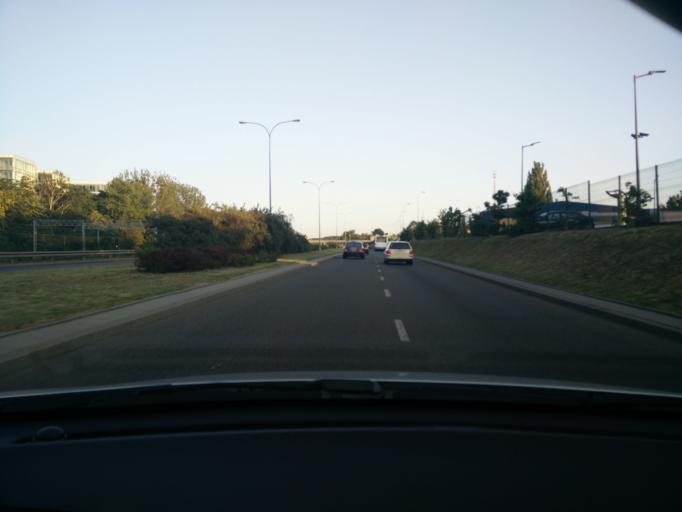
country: PL
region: Pomeranian Voivodeship
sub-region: Gdynia
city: Gdynia
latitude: 54.4947
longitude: 18.5362
